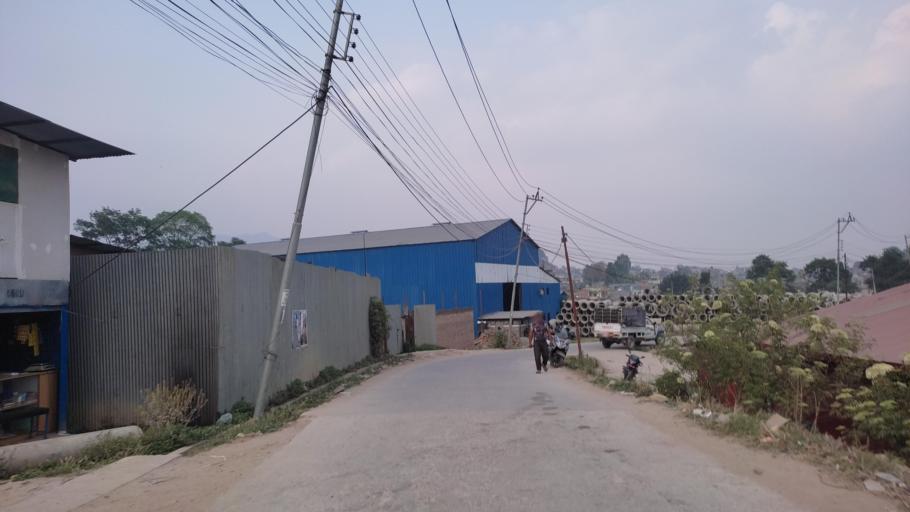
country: NP
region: Central Region
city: Kirtipur
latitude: 27.6803
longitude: 85.2535
